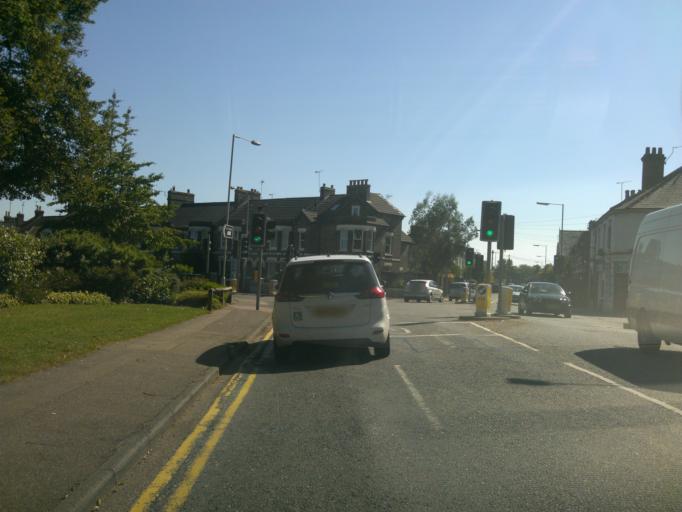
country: GB
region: England
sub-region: Essex
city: Colchester
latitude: 51.8810
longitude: 0.9140
